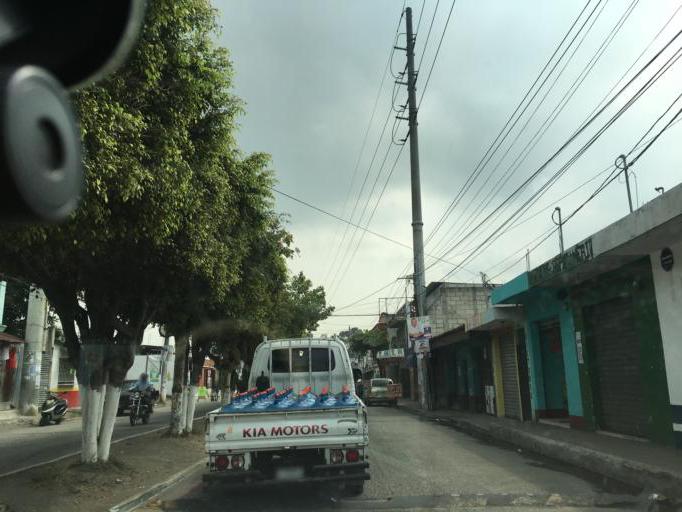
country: GT
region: Guatemala
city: Petapa
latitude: 14.5037
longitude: -90.5607
